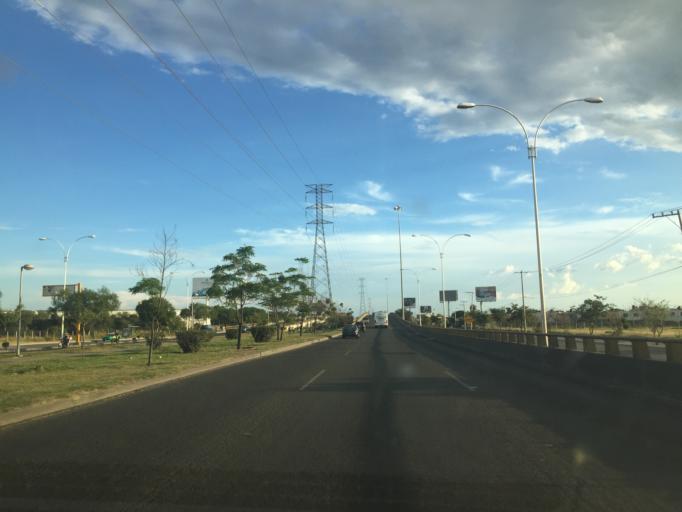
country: MX
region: Guanajuato
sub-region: Leon
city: Medina
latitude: 21.1169
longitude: -101.6265
